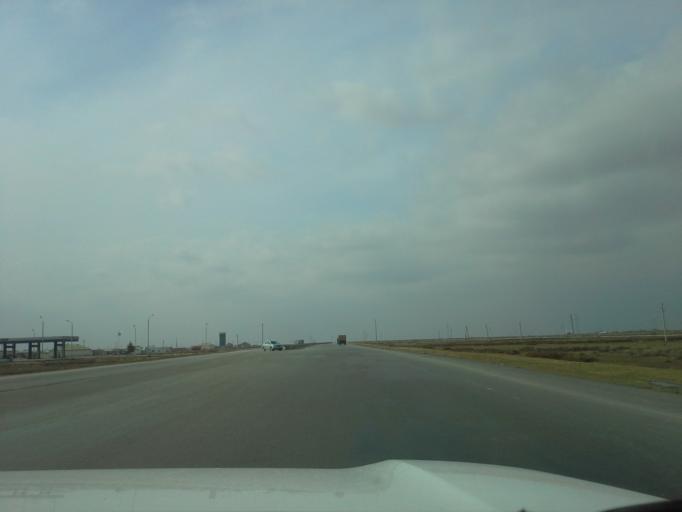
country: IR
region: Razavi Khorasan
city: Kalat-e Naderi
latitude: 37.2061
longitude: 60.0266
